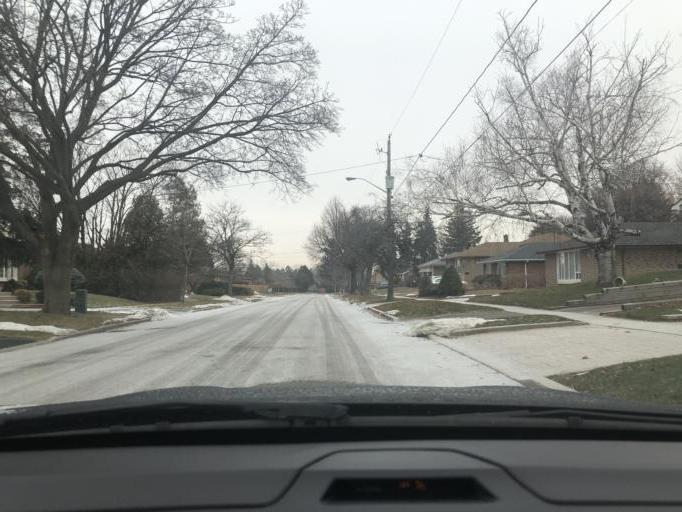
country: CA
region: Ontario
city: Scarborough
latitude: 43.7809
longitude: -79.2710
